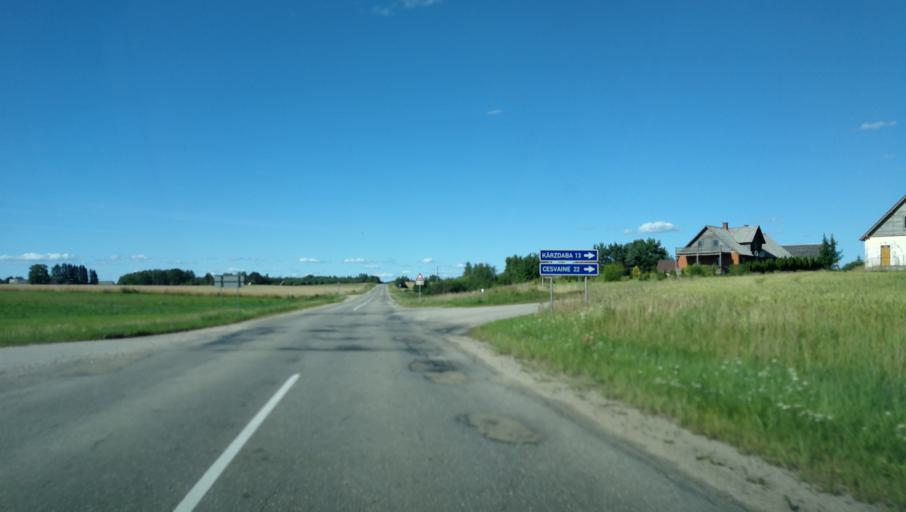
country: LV
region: Madonas Rajons
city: Madona
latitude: 56.9450
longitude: 26.0385
